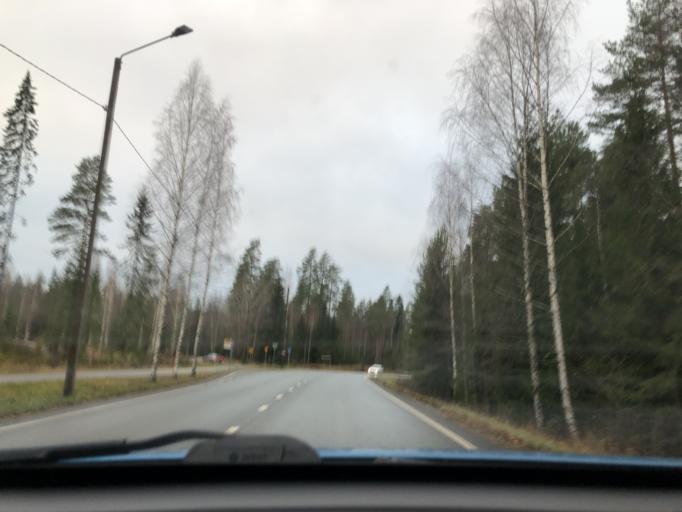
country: FI
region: Pirkanmaa
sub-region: Tampere
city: Kangasala
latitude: 61.5304
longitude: 24.0012
